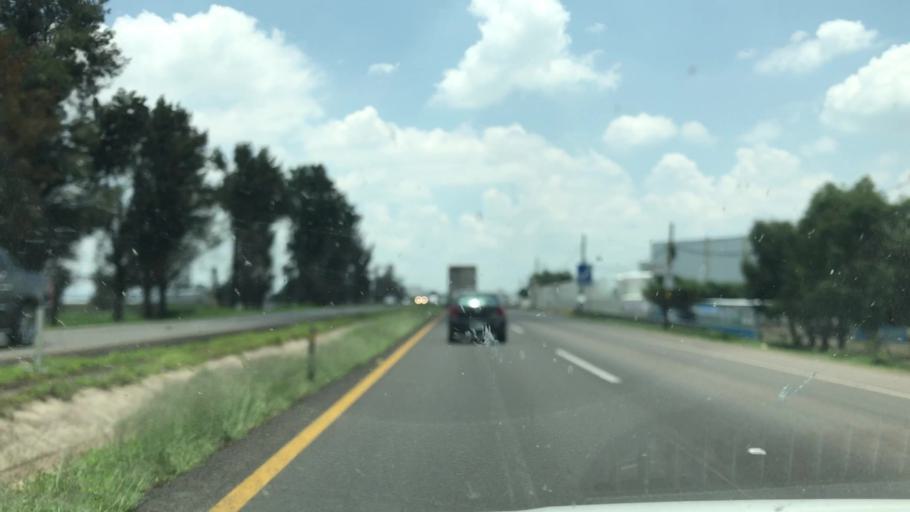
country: MX
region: Guanajuato
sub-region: Irapuato
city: San Jose de Bernalejo (El Guayabo)
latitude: 20.6165
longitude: -101.4034
